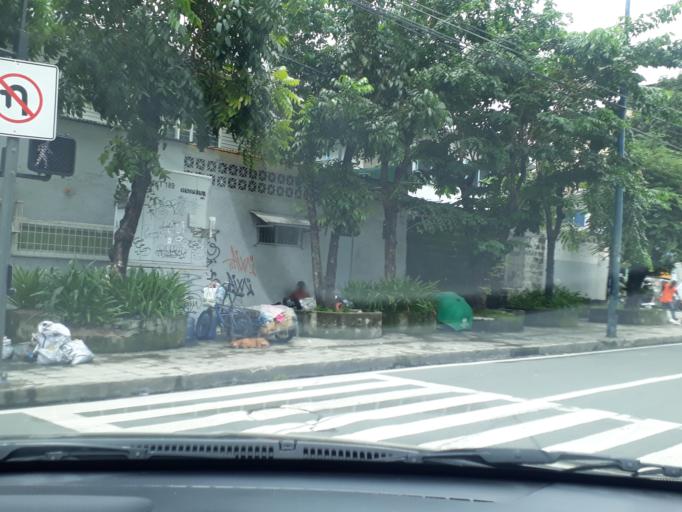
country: PH
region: Metro Manila
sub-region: Makati City
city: Makati City
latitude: 14.5684
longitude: 121.0182
